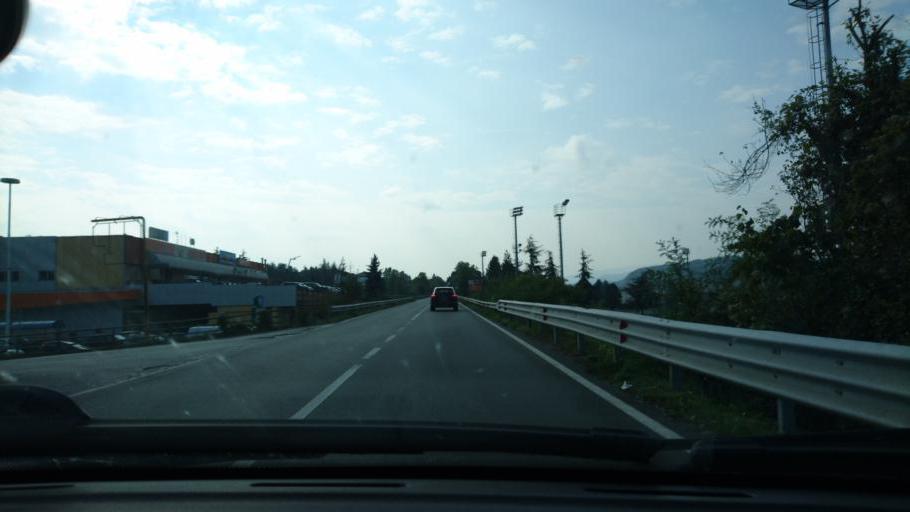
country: IT
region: Liguria
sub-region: Provincia di Savona
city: Cairo Montenotte
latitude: 44.4047
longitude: 8.2841
